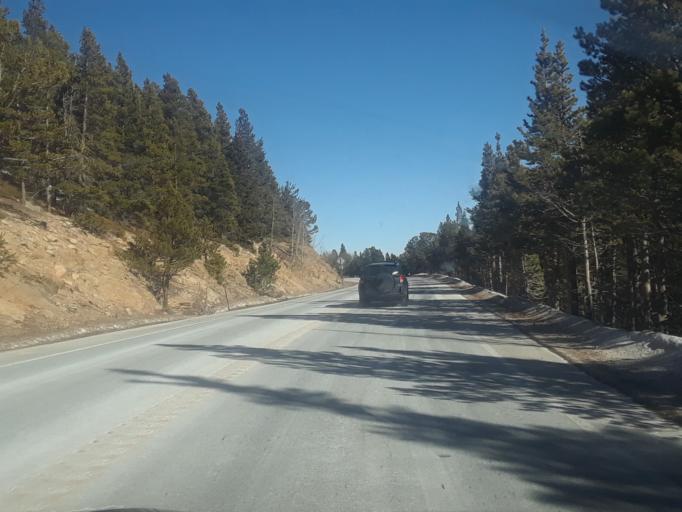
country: US
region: Colorado
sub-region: Boulder County
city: Nederland
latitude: 40.0795
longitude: -105.5017
